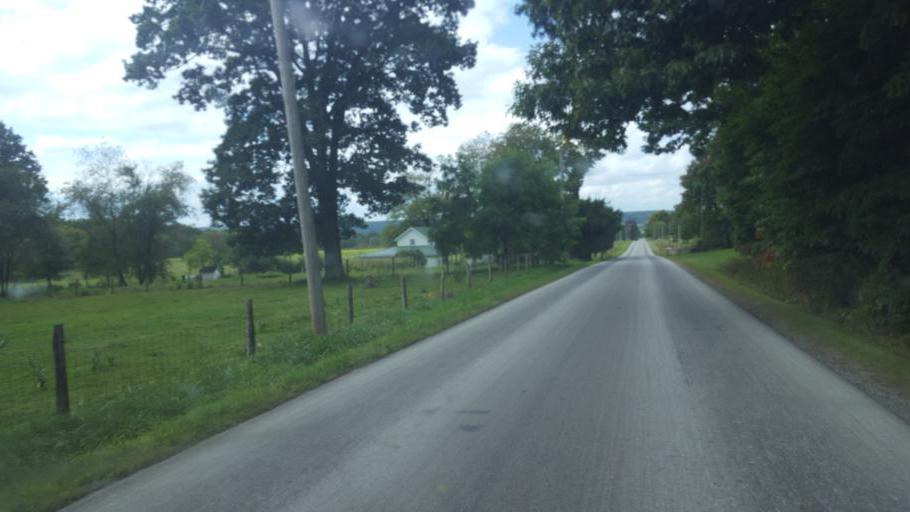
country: US
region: Pennsylvania
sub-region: Mercer County
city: Greenville
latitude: 41.5045
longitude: -80.3282
